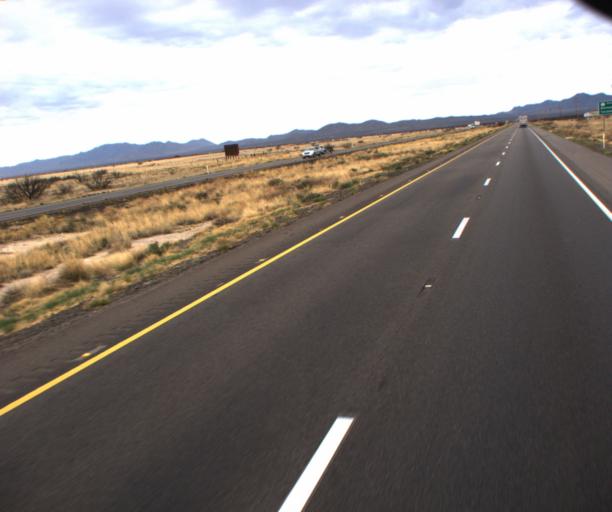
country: US
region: Arizona
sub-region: Cochise County
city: Willcox
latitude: 32.2111
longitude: -109.8915
